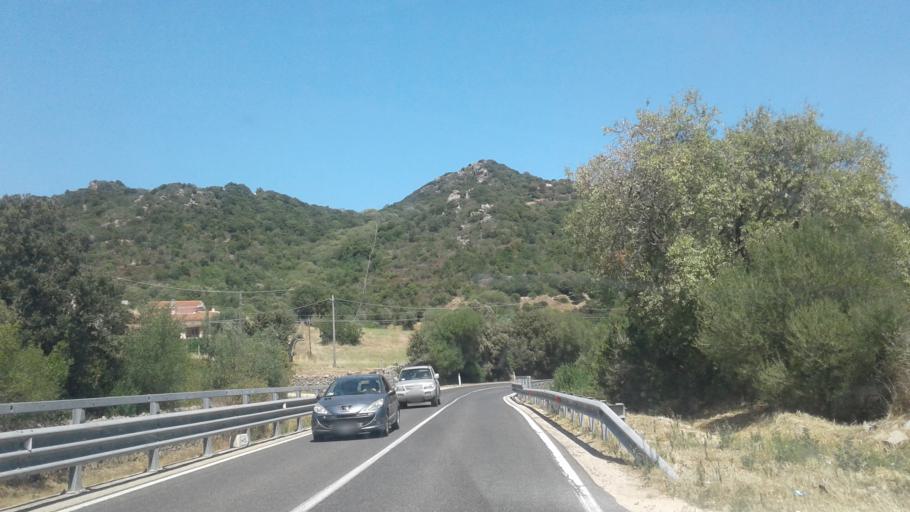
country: IT
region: Sardinia
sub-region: Provincia di Olbia-Tempio
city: Telti
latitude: 40.9041
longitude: 9.3938
